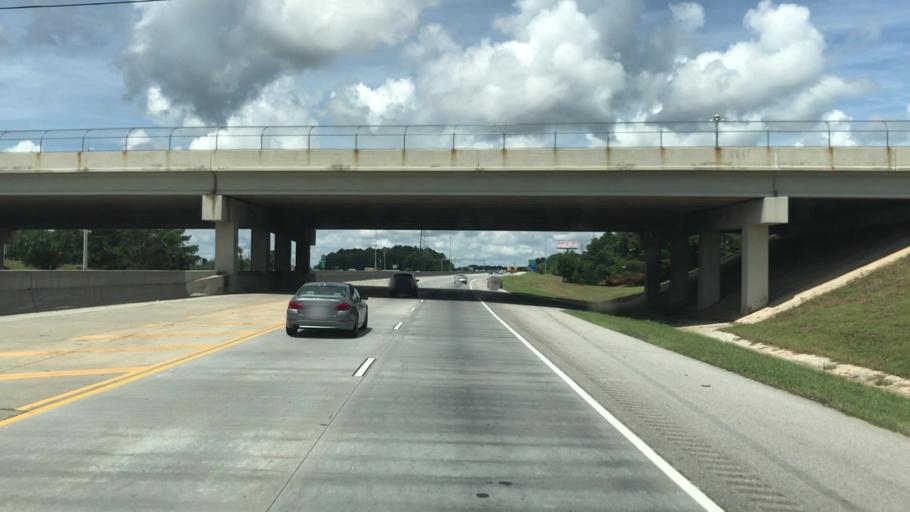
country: US
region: Georgia
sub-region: Newton County
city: Covington
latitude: 33.6127
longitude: -83.8242
